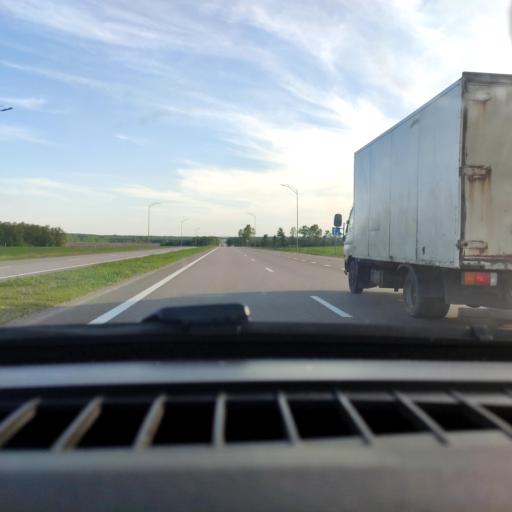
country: RU
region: Belgorod
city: Staryy Oskol
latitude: 51.4196
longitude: 37.8905
